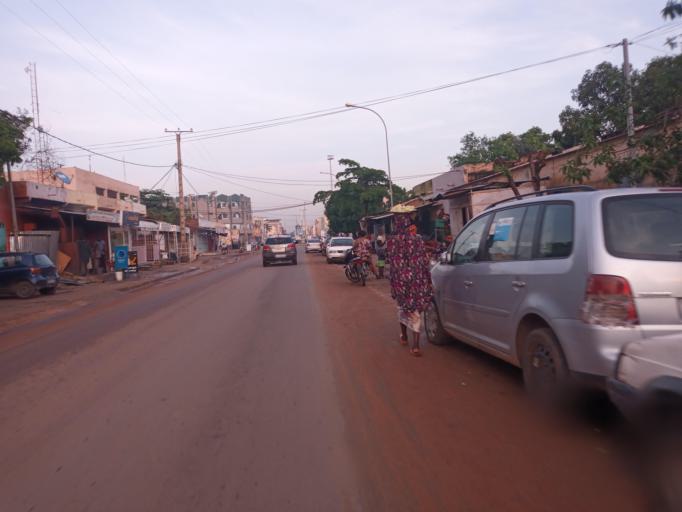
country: ML
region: Bamako
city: Bamako
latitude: 12.6280
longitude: -8.0367
